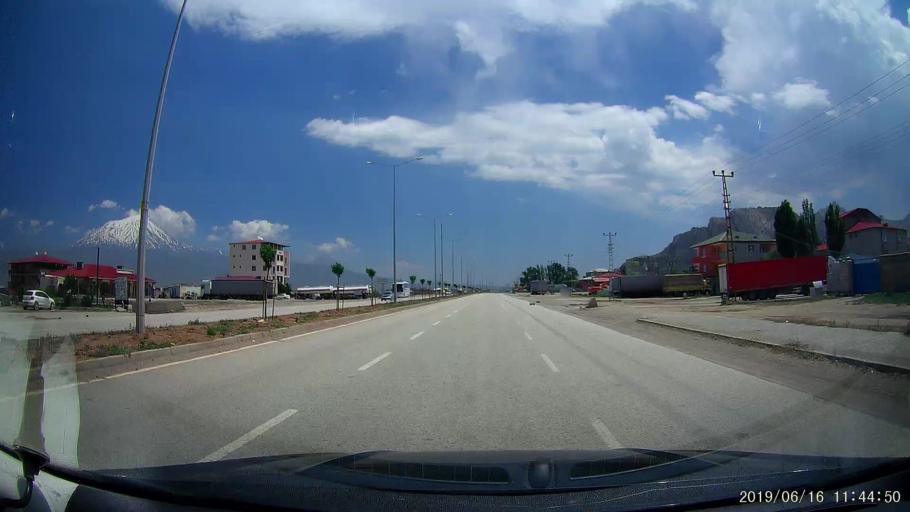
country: TR
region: Agri
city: Dogubayazit
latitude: 39.5574
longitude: 44.0943
